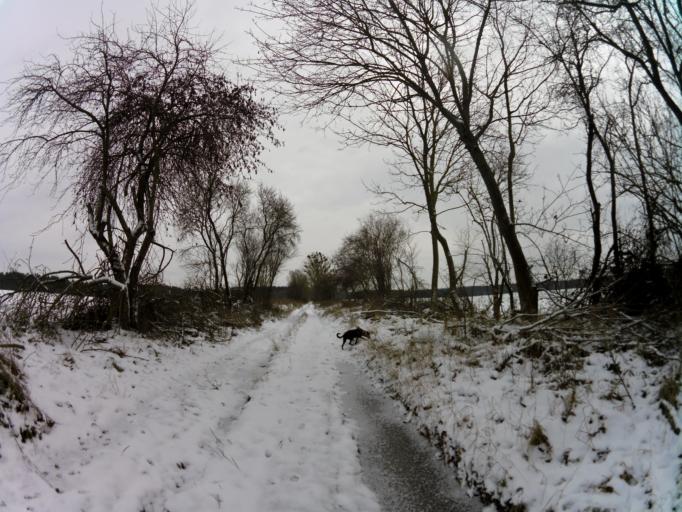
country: PL
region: West Pomeranian Voivodeship
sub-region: Powiat choszczenski
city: Recz
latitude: 53.2709
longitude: 15.5236
